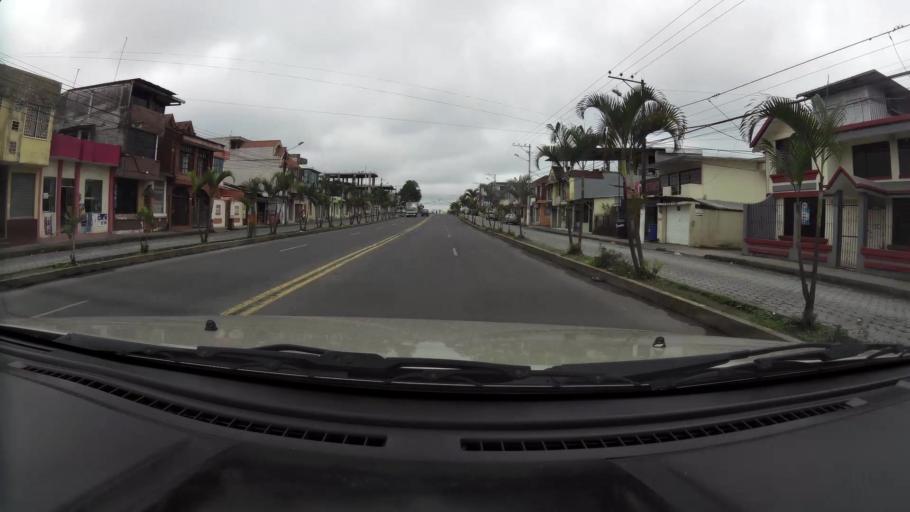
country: EC
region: Santo Domingo de los Tsachilas
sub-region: Canton Santo Domingo de los Colorados
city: Santo Domingo de los Colorados
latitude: -0.2433
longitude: -79.1837
